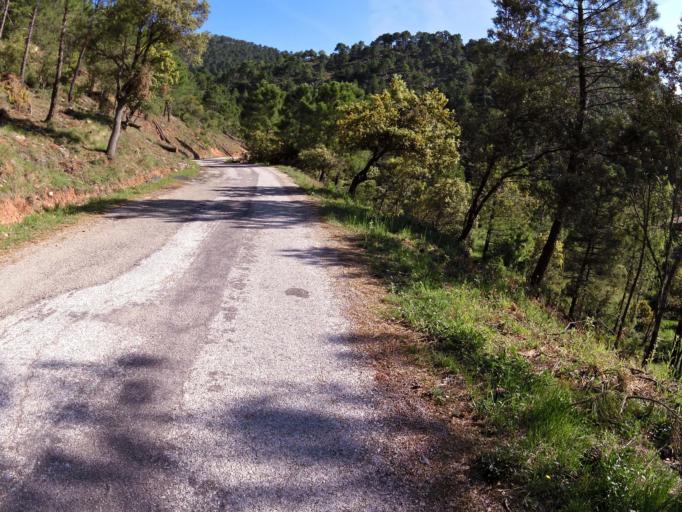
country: ES
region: Castille-La Mancha
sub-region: Provincia de Albacete
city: Riopar
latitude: 38.5218
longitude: -2.4557
